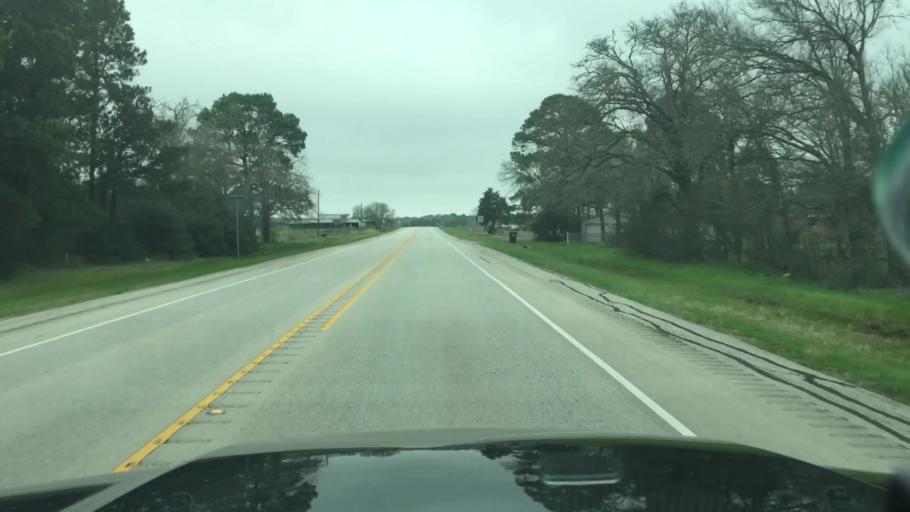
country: US
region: Texas
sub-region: Lee County
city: Giddings
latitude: 30.0584
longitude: -96.9148
